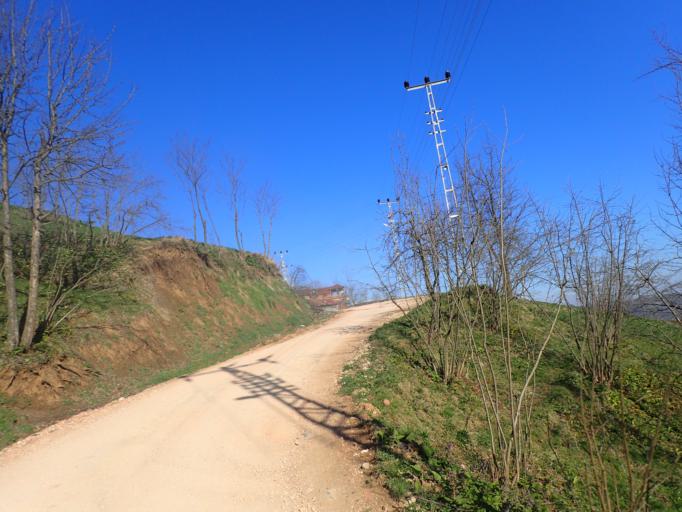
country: TR
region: Ordu
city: Camas
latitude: 40.8711
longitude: 37.5019
